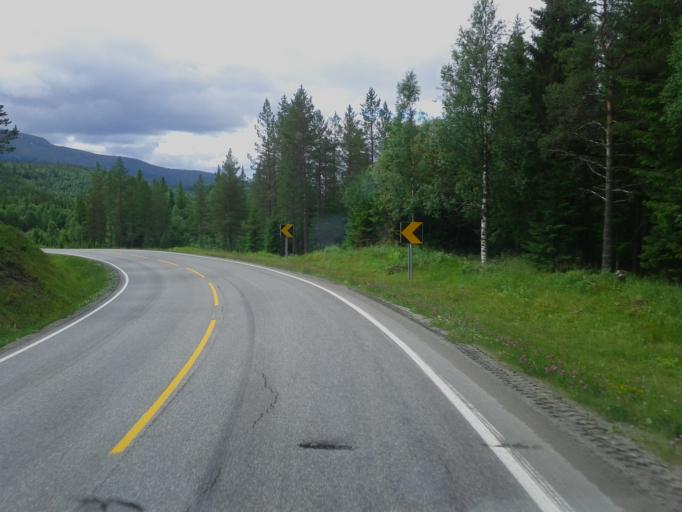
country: NO
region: Nord-Trondelag
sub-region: Hoylandet
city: Hoylandet
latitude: 64.6477
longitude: 12.6362
